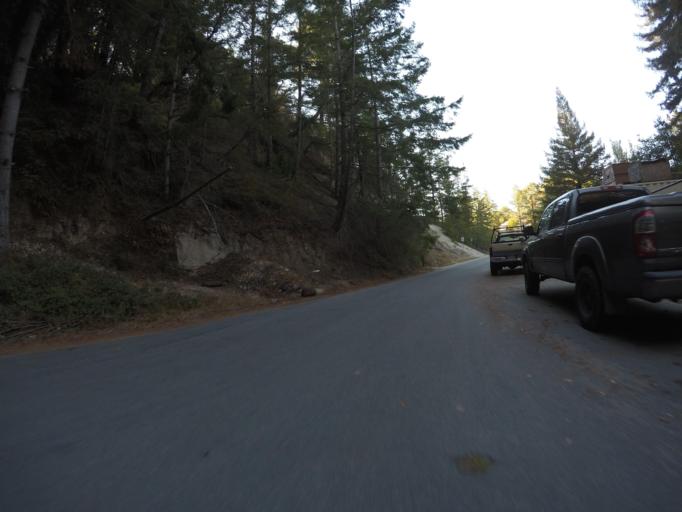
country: US
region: California
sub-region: Santa Cruz County
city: Scotts Valley
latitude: 37.0369
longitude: -122.0334
